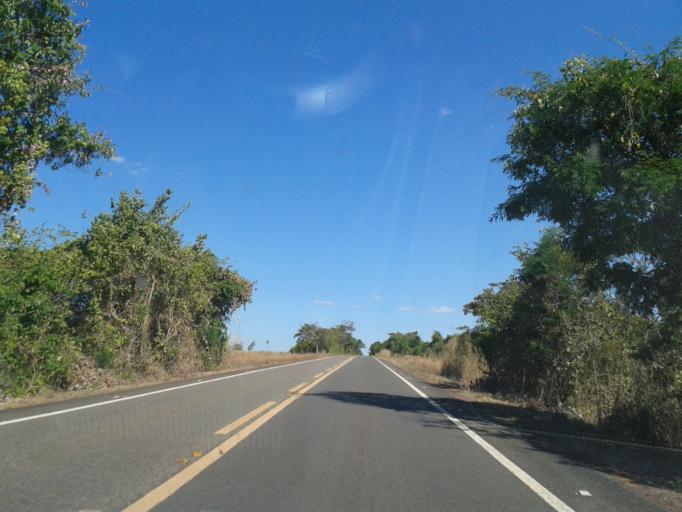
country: BR
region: Goias
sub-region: Sao Miguel Do Araguaia
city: Sao Miguel do Araguaia
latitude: -13.7121
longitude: -50.3333
